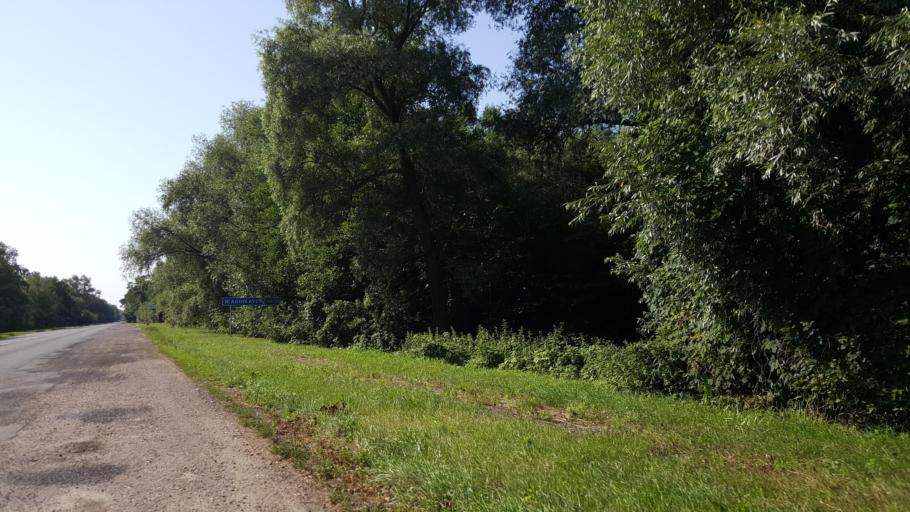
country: BY
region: Brest
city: Zhabinka
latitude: 52.2981
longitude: 23.9358
